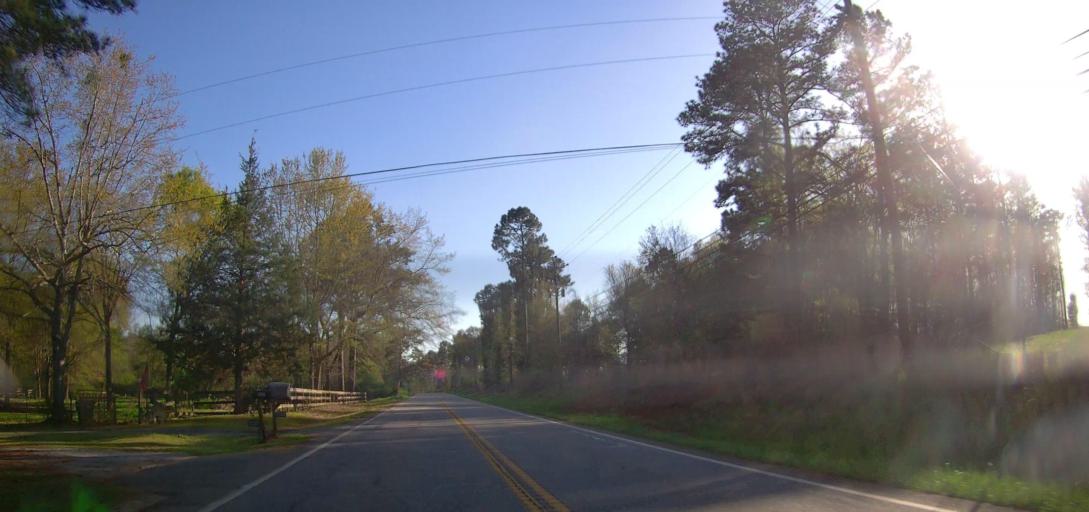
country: US
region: Georgia
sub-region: Butts County
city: Indian Springs
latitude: 33.2577
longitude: -83.9107
